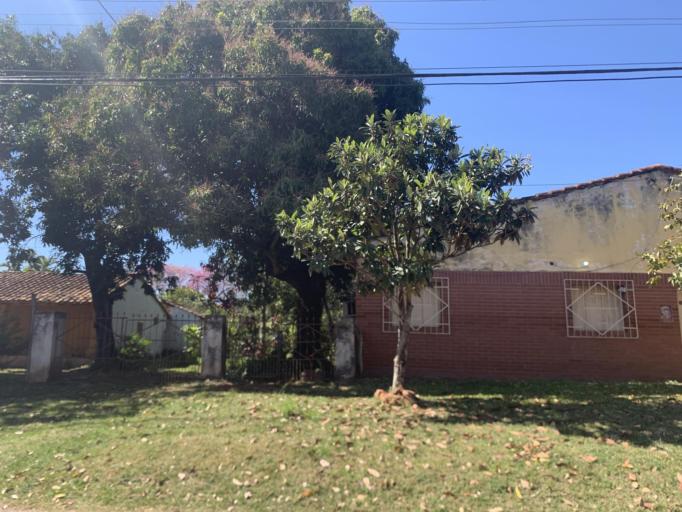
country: PY
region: Misiones
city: San Juan Bautista
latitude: -26.6710
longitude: -57.1486
